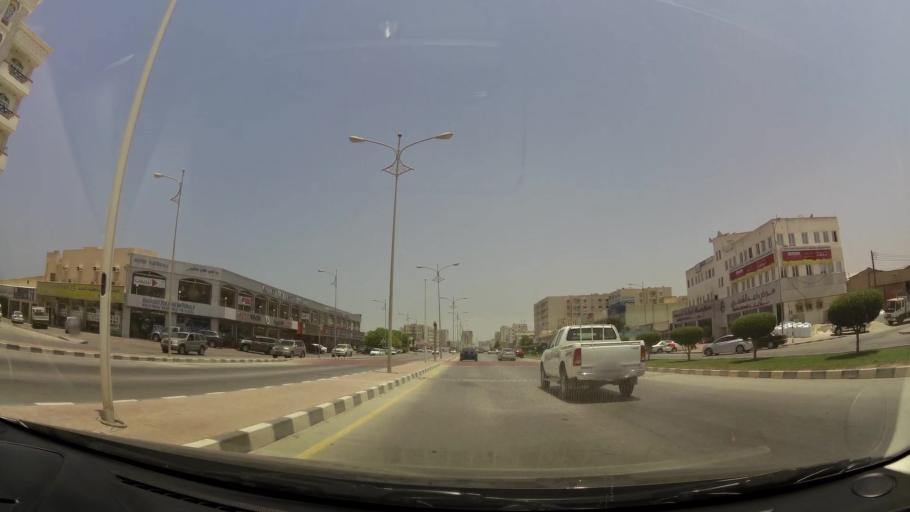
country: OM
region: Zufar
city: Salalah
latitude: 17.0201
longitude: 54.1142
